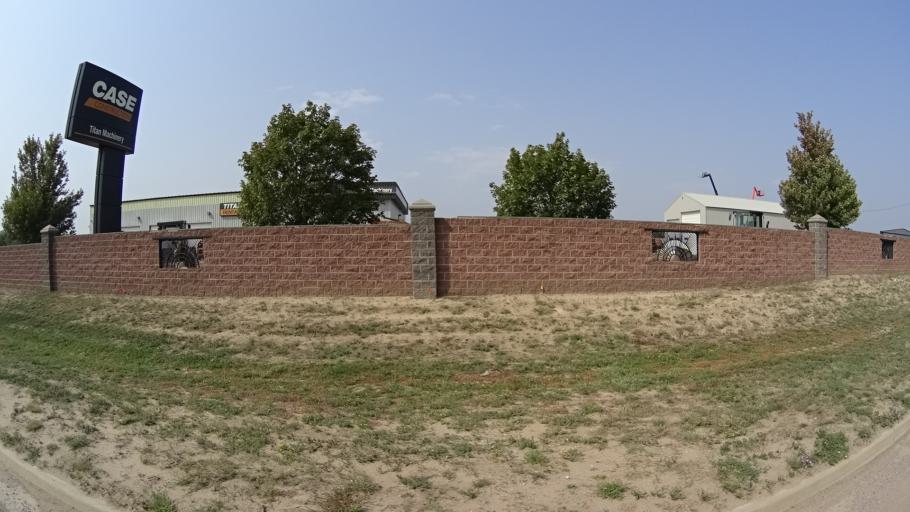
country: US
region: Colorado
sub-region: El Paso County
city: Cimarron Hills
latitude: 38.8331
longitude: -104.7248
